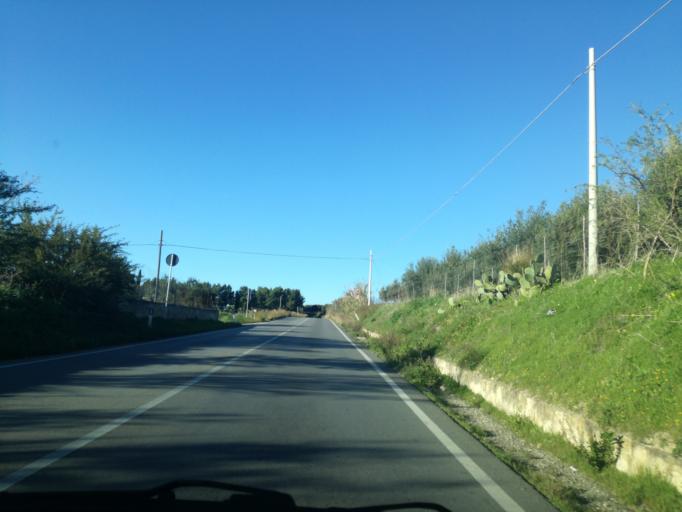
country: IT
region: Sicily
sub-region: Provincia di Caltanissetta
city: Gela
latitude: 37.1086
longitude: 14.1602
